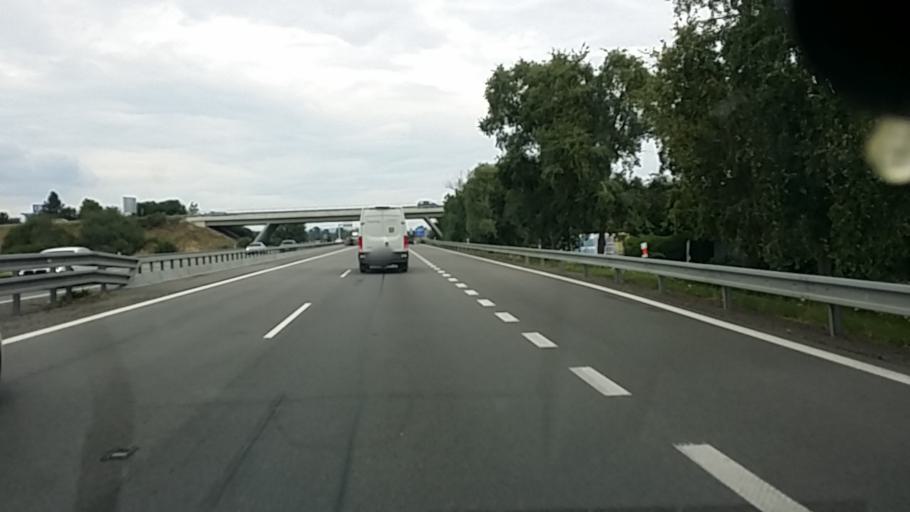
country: CZ
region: South Moravian
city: Modrice
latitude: 49.1338
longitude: 16.6385
